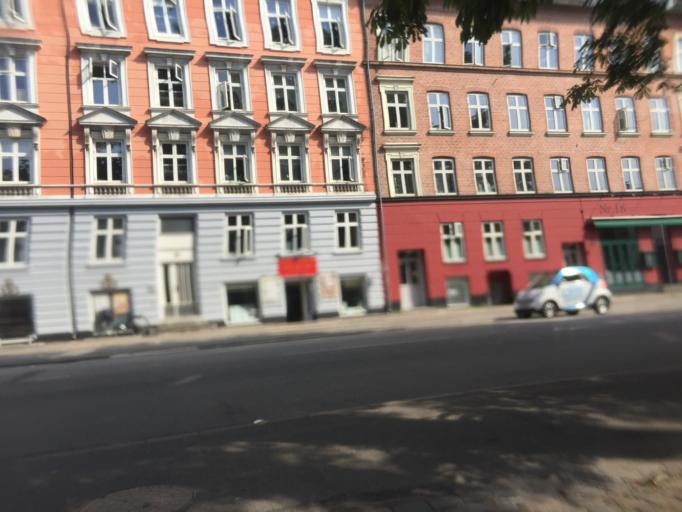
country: DK
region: Capital Region
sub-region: Kobenhavn
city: Copenhagen
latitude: 55.6910
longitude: 12.5755
